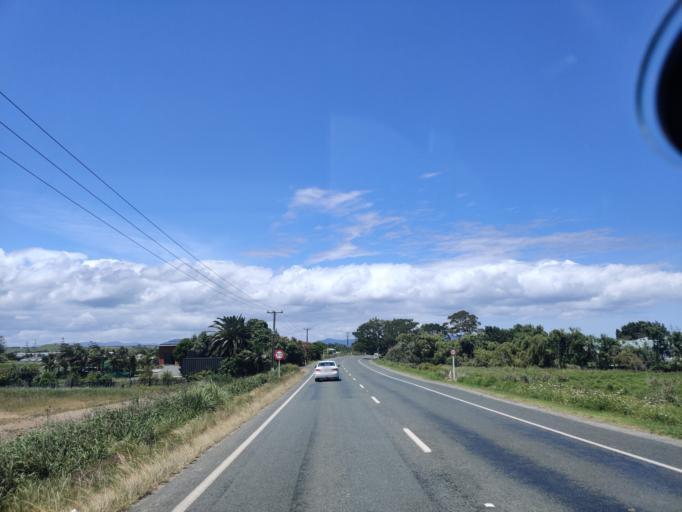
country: NZ
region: Northland
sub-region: Far North District
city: Kaitaia
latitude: -35.0423
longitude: 173.2562
